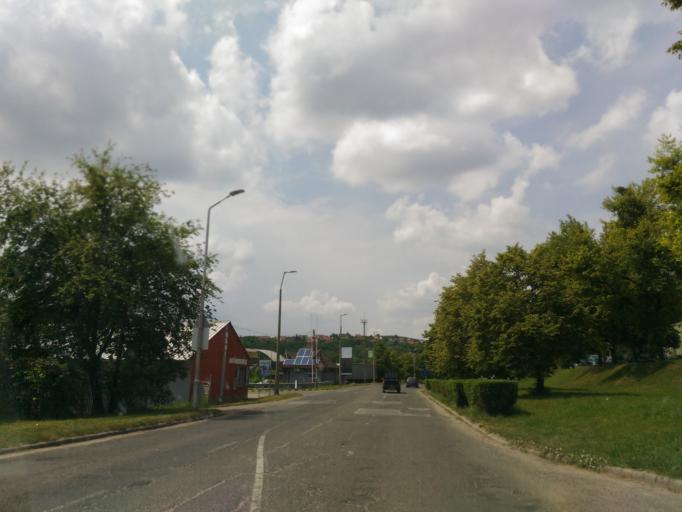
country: HU
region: Baranya
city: Komlo
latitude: 46.1933
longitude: 18.2556
